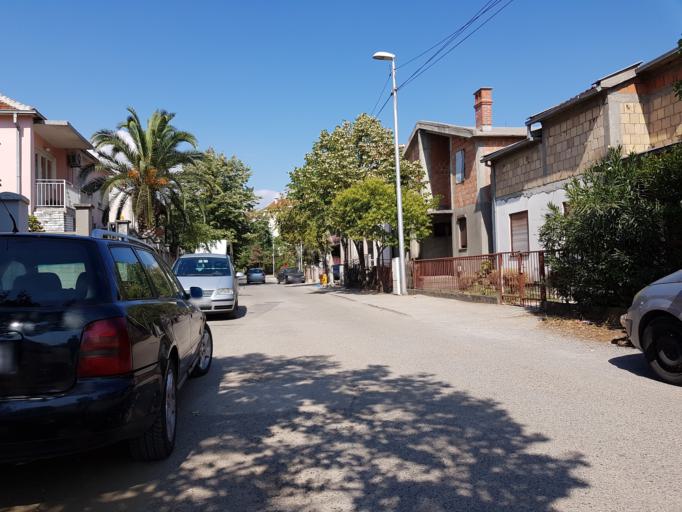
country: ME
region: Podgorica
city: Podgorica
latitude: 42.4307
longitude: 19.2776
